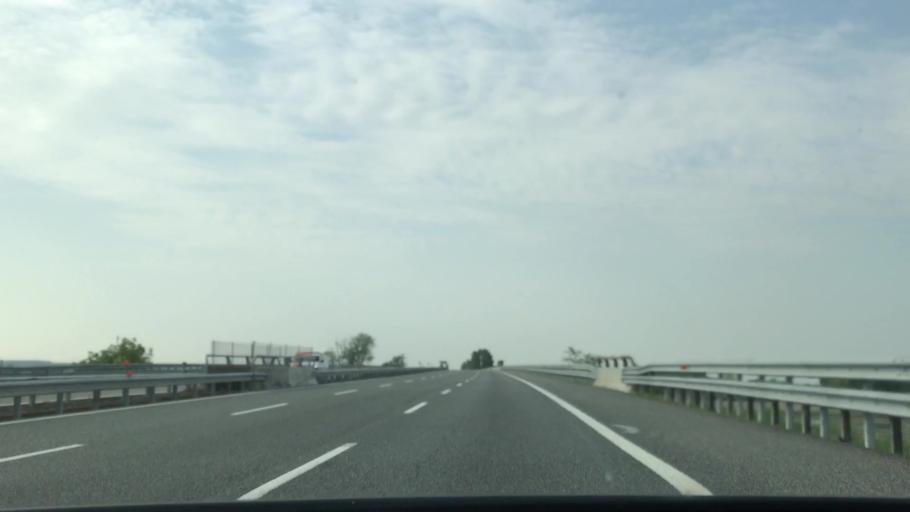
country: IT
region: Piedmont
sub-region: Provincia di Vercelli
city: Borgo Vercelli
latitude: 45.3328
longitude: 8.4715
